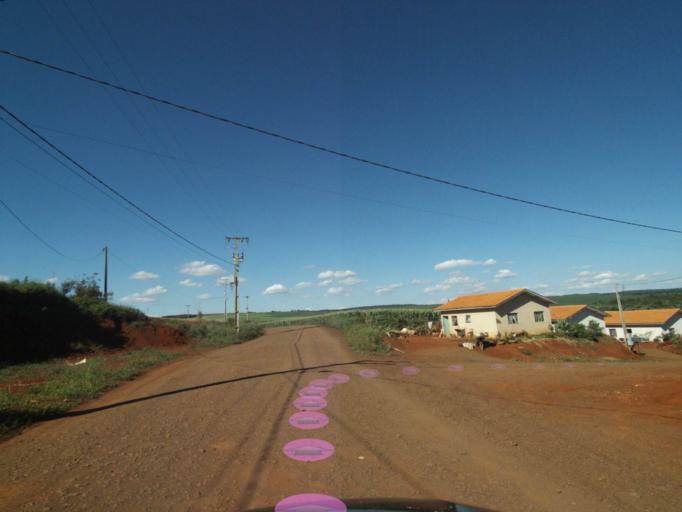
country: BR
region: Parana
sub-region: Coronel Vivida
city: Coronel Vivida
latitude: -26.1365
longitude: -52.3932
